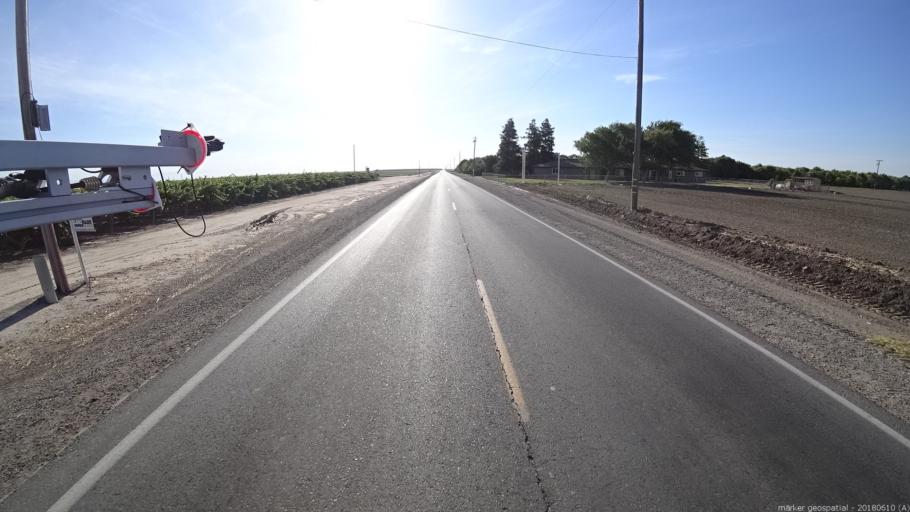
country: US
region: California
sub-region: Madera County
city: Fairmead
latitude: 36.9528
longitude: -120.2837
